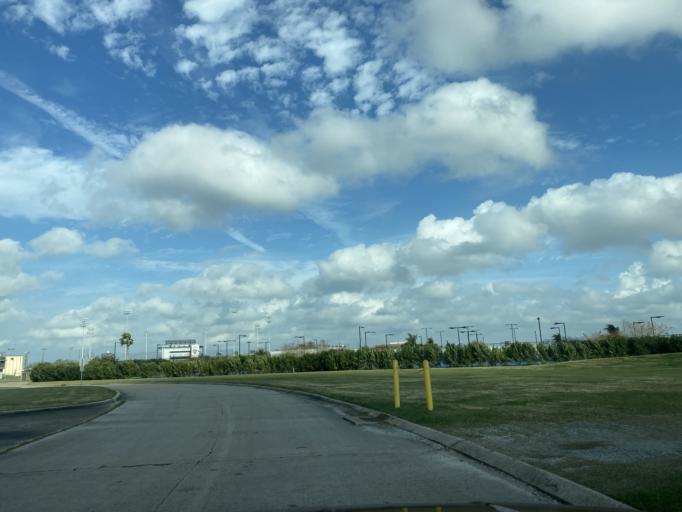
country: US
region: Louisiana
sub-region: Orleans Parish
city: New Orleans
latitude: 30.0281
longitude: -90.0497
